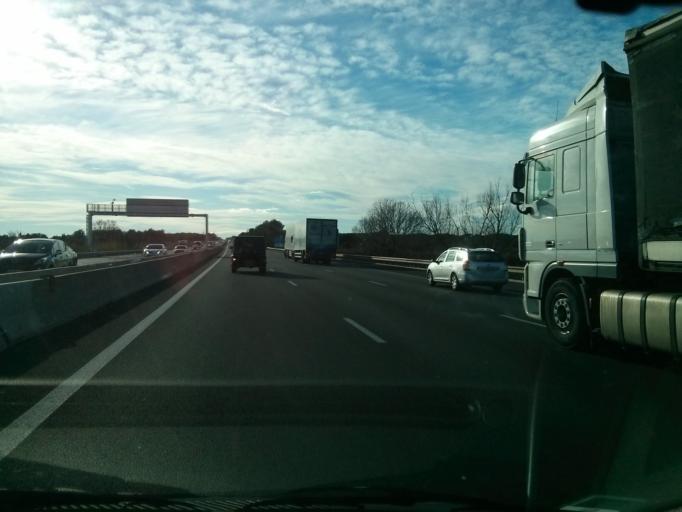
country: FR
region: Languedoc-Roussillon
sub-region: Departement de l'Herault
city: Villetelle
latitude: 43.7196
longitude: 4.1420
